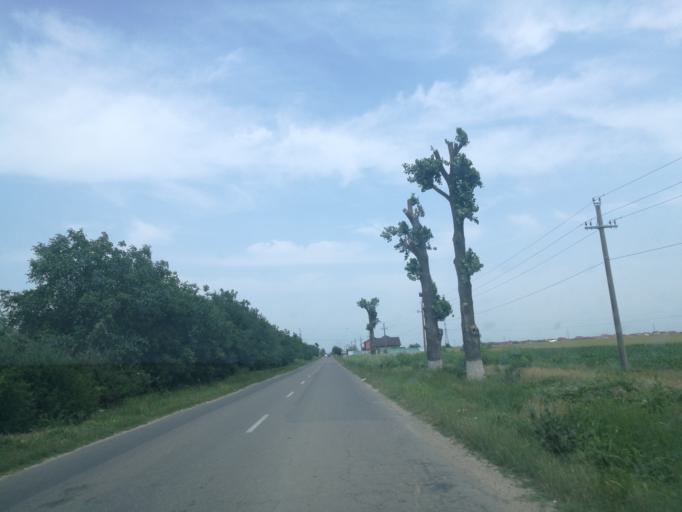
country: RO
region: Ilfov
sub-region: Comuna Vidra
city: Vidra
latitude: 44.2720
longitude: 26.1719
